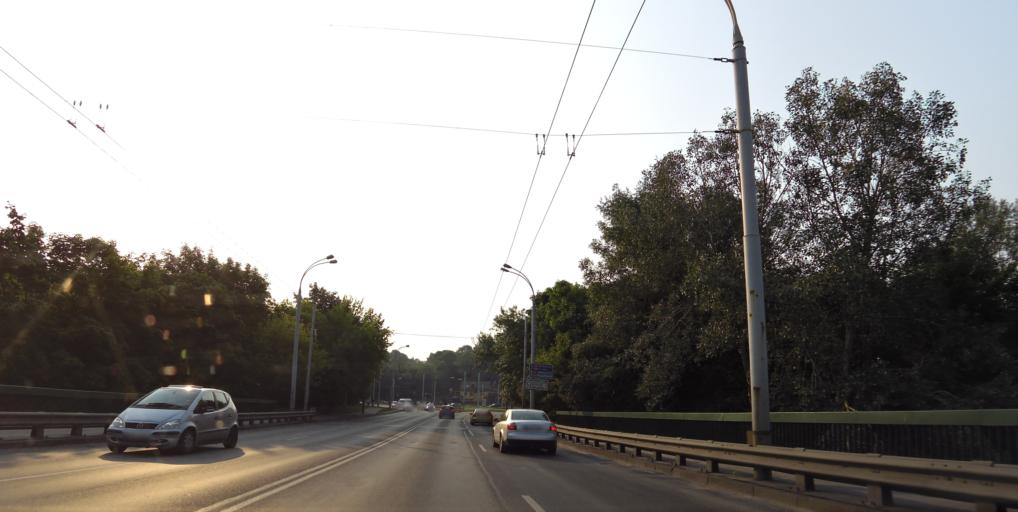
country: LT
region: Vilnius County
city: Rasos
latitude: 54.6944
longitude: 25.3024
